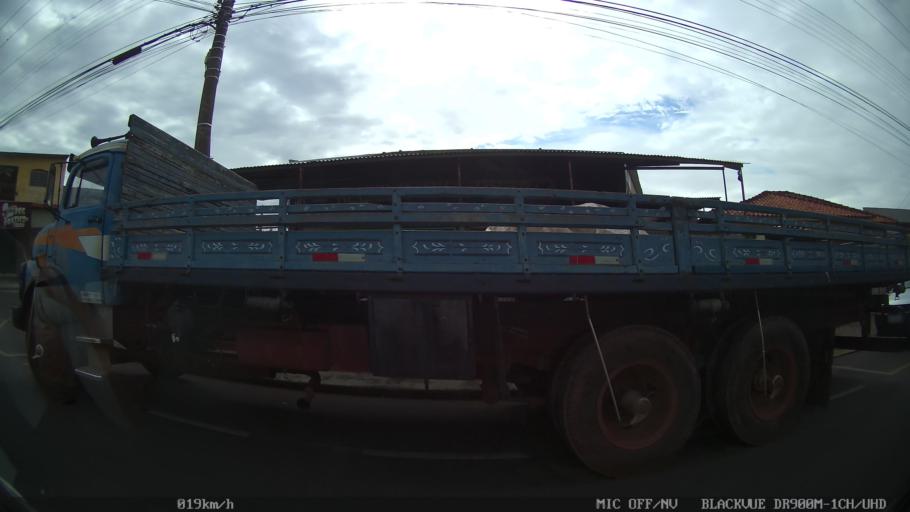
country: BR
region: Sao Paulo
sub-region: Sao Jose Do Rio Preto
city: Sao Jose do Rio Preto
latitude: -20.8201
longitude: -49.3543
